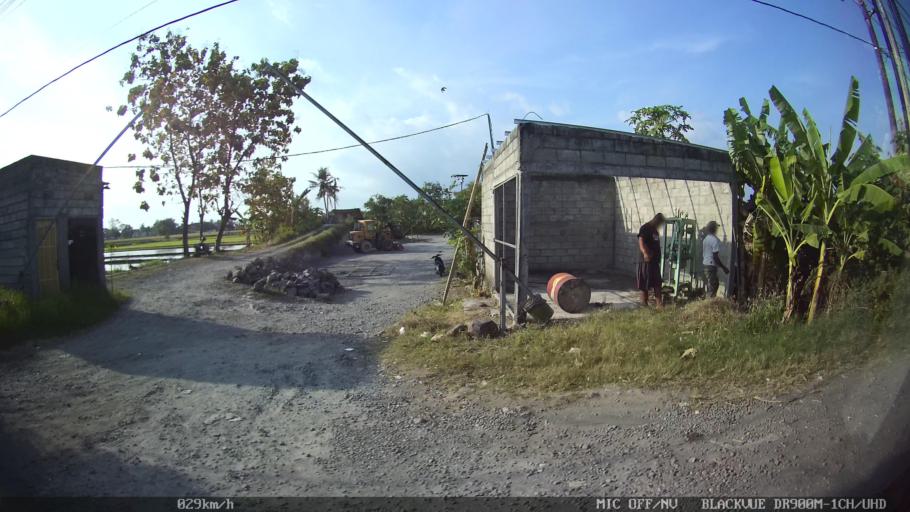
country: ID
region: Daerah Istimewa Yogyakarta
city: Sewon
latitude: -7.8674
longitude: 110.3468
